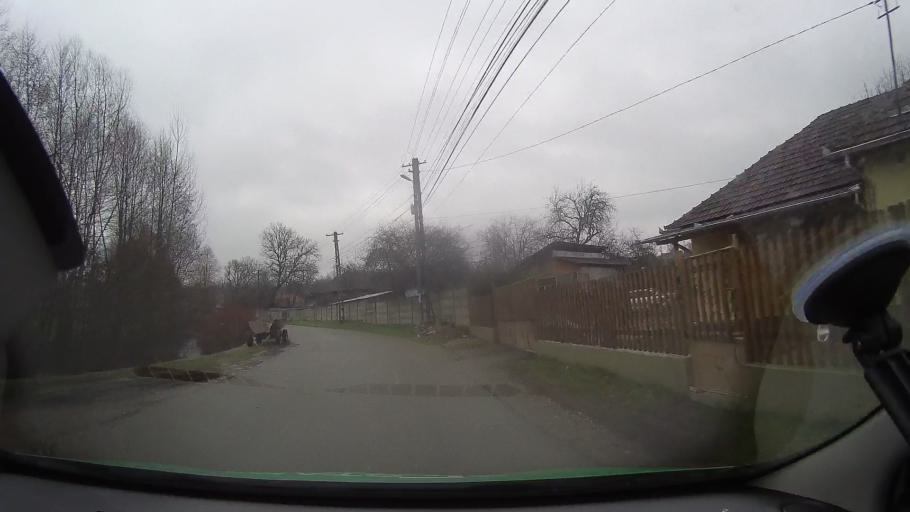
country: RO
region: Arad
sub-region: Comuna Halmagel
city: Halmagel
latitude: 46.2681
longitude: 22.6215
